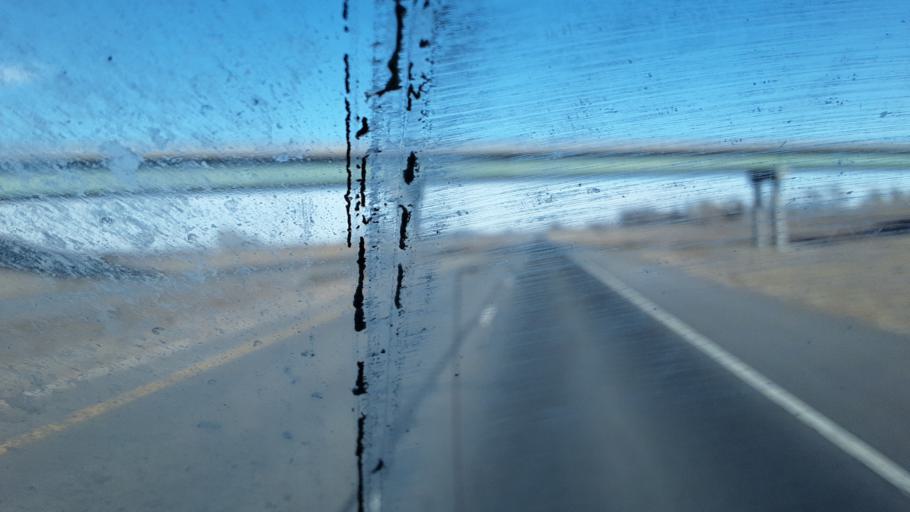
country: US
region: Colorado
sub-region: Weld County
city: Lochbuie
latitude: 40.0143
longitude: -104.6999
